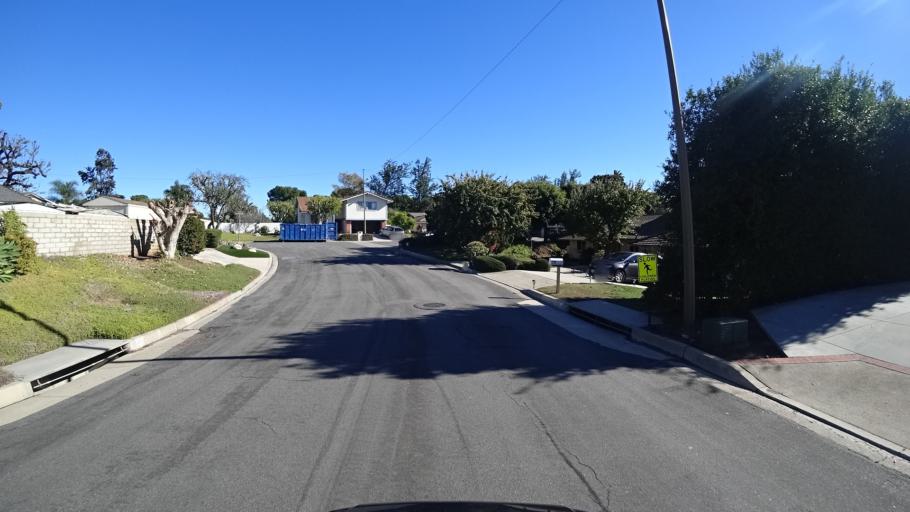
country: US
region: California
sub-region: Orange County
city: Yorba Linda
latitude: 33.8868
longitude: -117.8001
